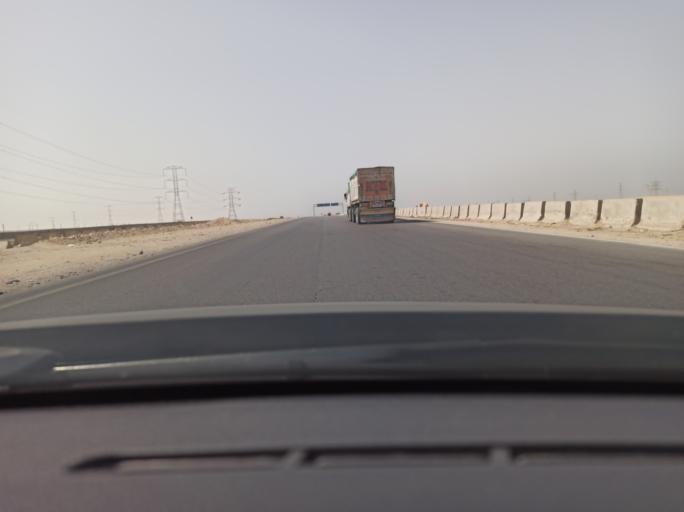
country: EG
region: Muhafazat al Fayyum
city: Al Wasitah
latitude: 29.3894
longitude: 31.3210
